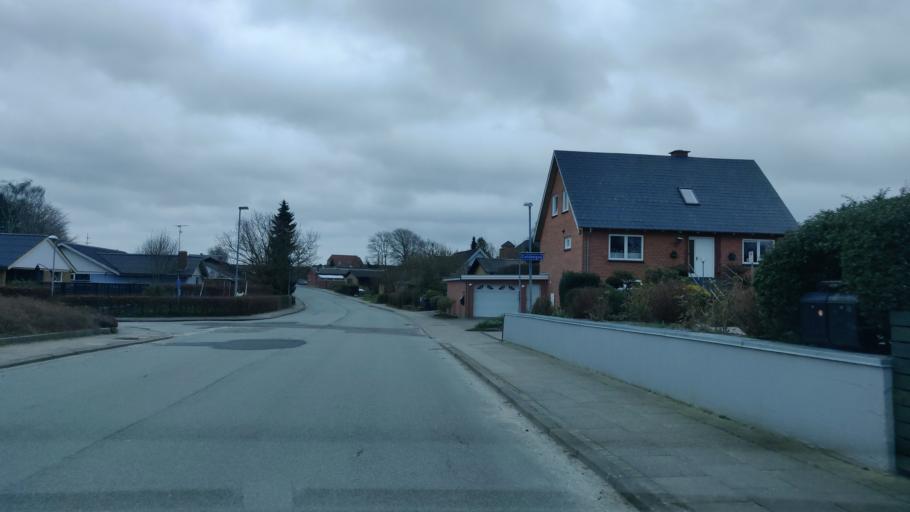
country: DK
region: Central Jutland
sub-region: Viborg Kommune
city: Stoholm
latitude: 56.4869
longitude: 9.1468
